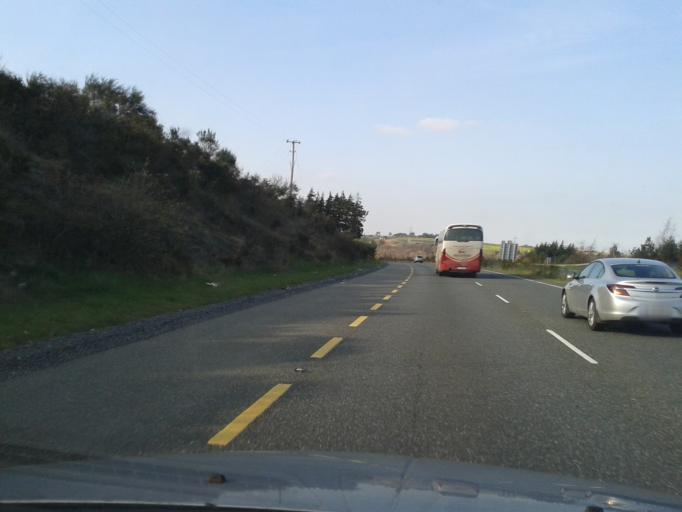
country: IE
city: Newtownmountkennedy
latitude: 53.0659
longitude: -6.0921
